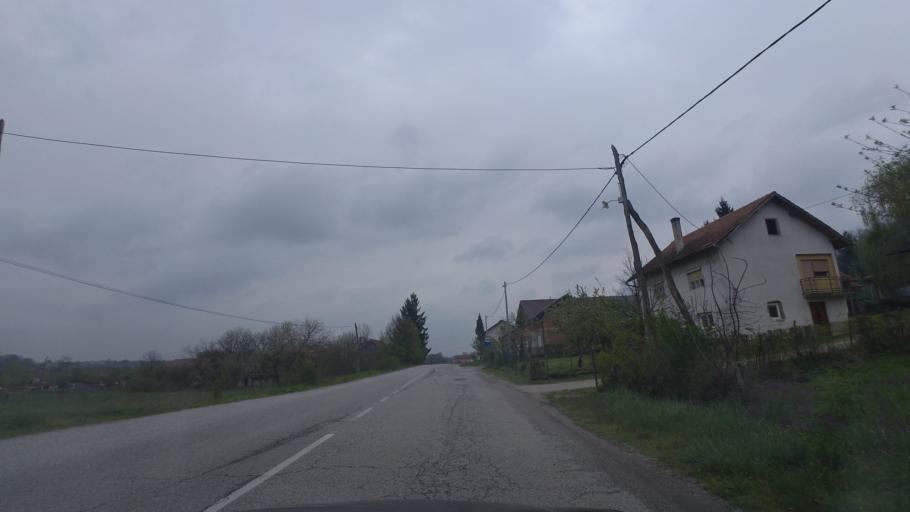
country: HR
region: Karlovacka
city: Ozalj
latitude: 45.6350
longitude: 15.5424
